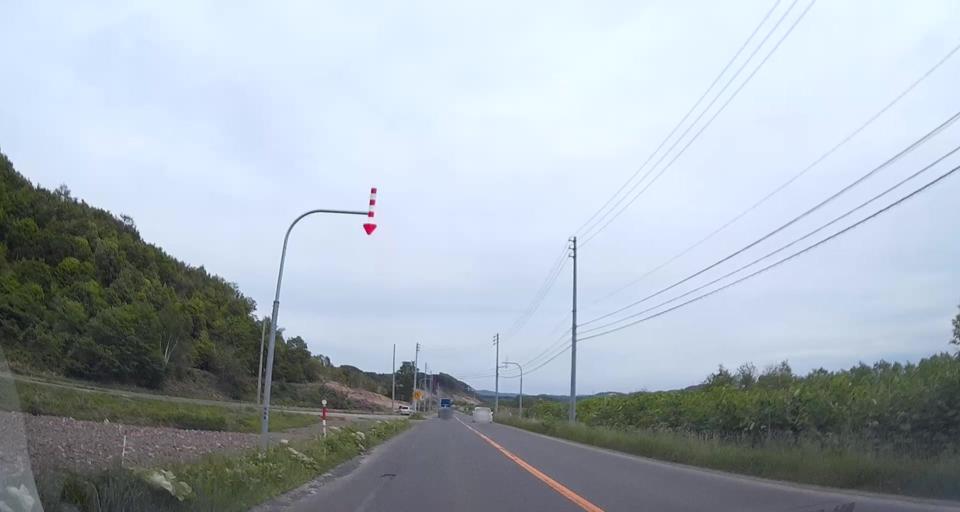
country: JP
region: Hokkaido
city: Chitose
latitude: 42.7403
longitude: 141.9039
